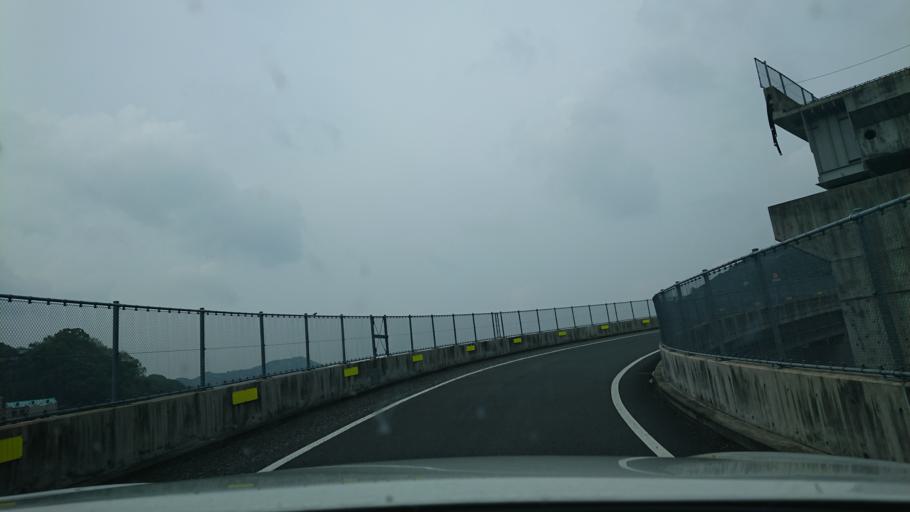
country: JP
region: Ehime
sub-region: Nishiuwa-gun
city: Ikata-cho
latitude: 33.4683
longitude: 132.4286
